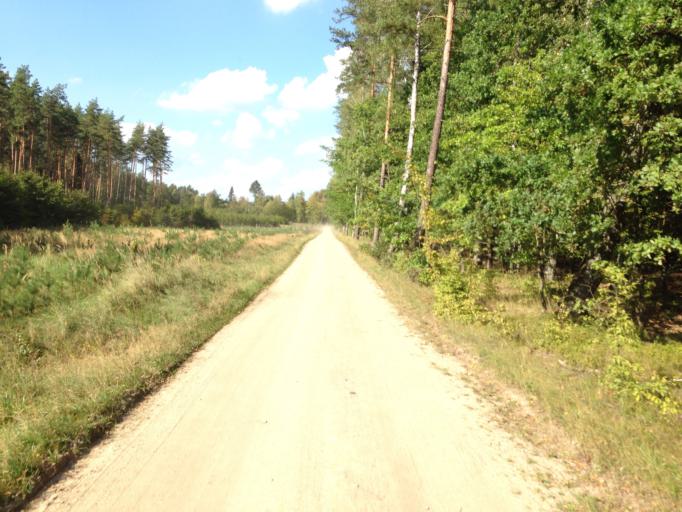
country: PL
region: Masovian Voivodeship
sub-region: Powiat zurominski
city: Lubowidz
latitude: 53.1648
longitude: 19.7558
